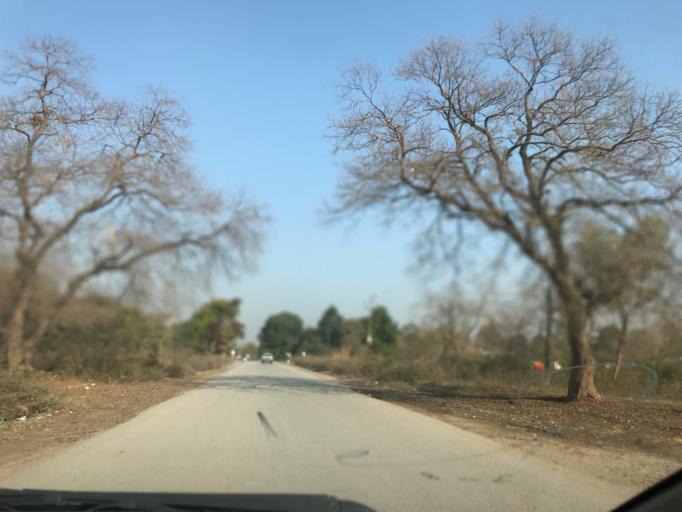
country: PK
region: Islamabad
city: Islamabad
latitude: 33.6798
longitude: 73.1432
